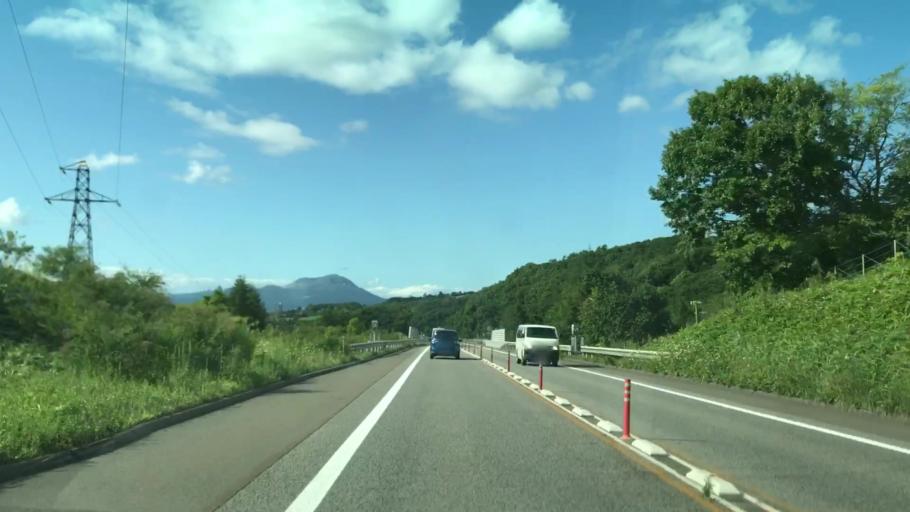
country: JP
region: Hokkaido
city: Date
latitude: 42.4268
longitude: 140.9273
